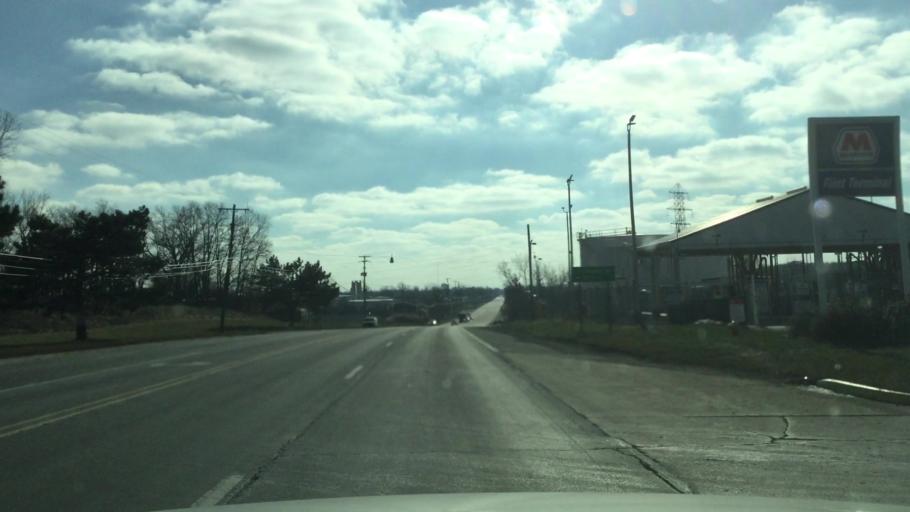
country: US
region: Michigan
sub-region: Genesee County
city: Beecher
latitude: 43.0921
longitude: -83.6747
